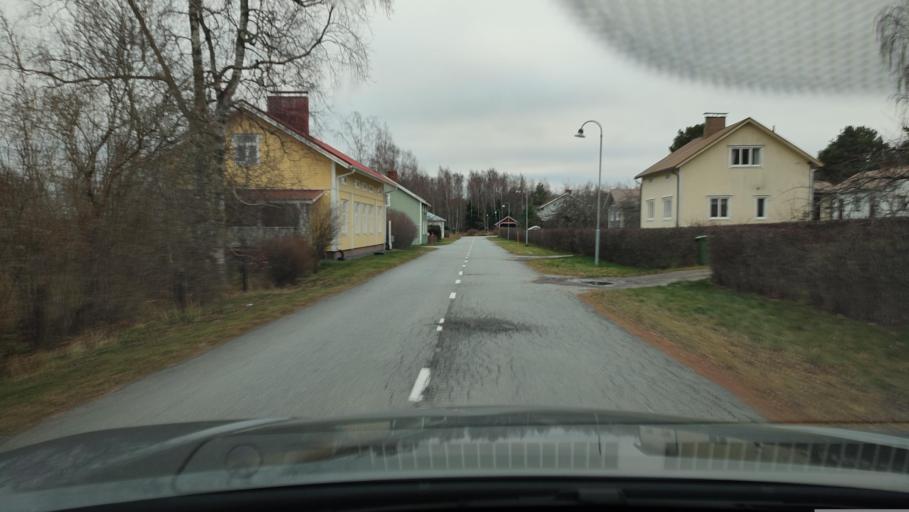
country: FI
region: Ostrobothnia
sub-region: Sydosterbotten
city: Kristinestad
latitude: 62.2678
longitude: 21.3727
